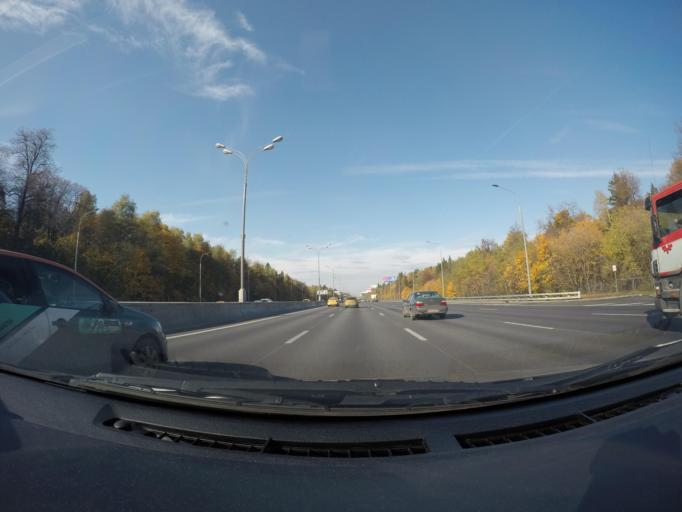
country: RU
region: Moscow
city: Gol'yanovo
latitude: 55.8465
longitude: 37.7960
